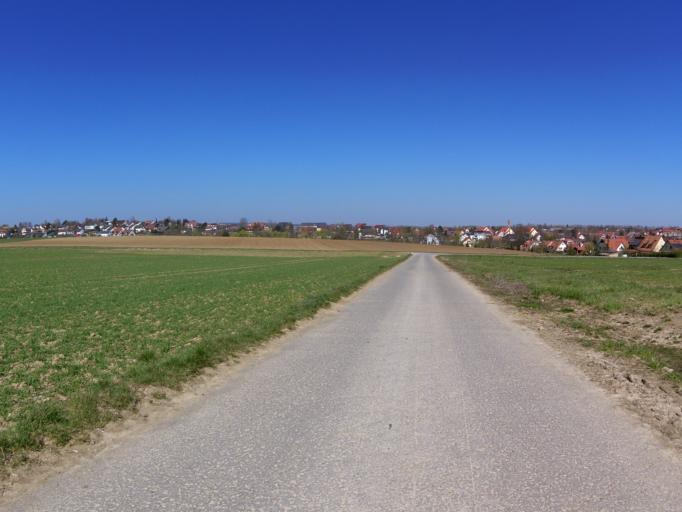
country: DE
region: Bavaria
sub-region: Regierungsbezirk Unterfranken
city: Kurnach
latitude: 49.8399
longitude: 10.0362
